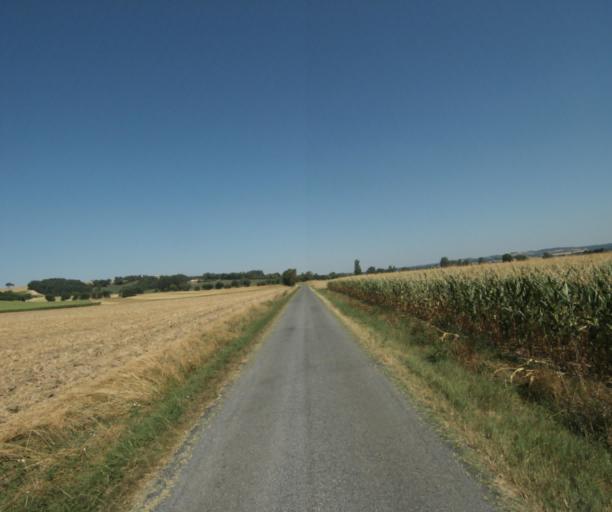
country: FR
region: Midi-Pyrenees
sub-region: Departement du Tarn
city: Puylaurens
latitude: 43.5222
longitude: 1.9423
